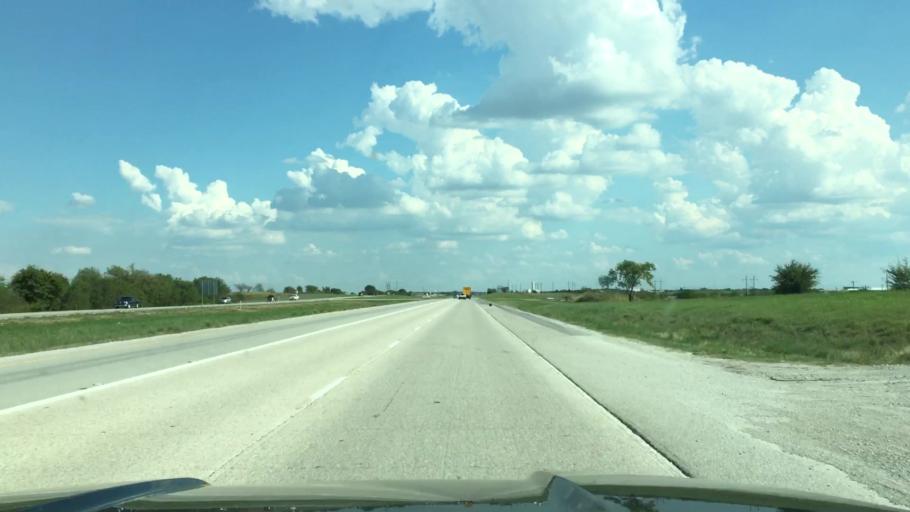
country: US
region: Texas
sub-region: Wise County
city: Decatur
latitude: 33.1891
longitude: -97.5559
